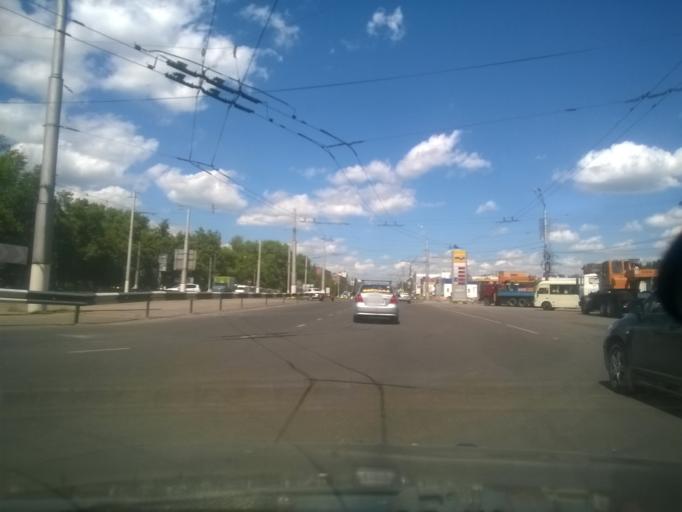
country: RU
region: Kursk
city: Kursk
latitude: 51.6627
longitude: 36.1375
